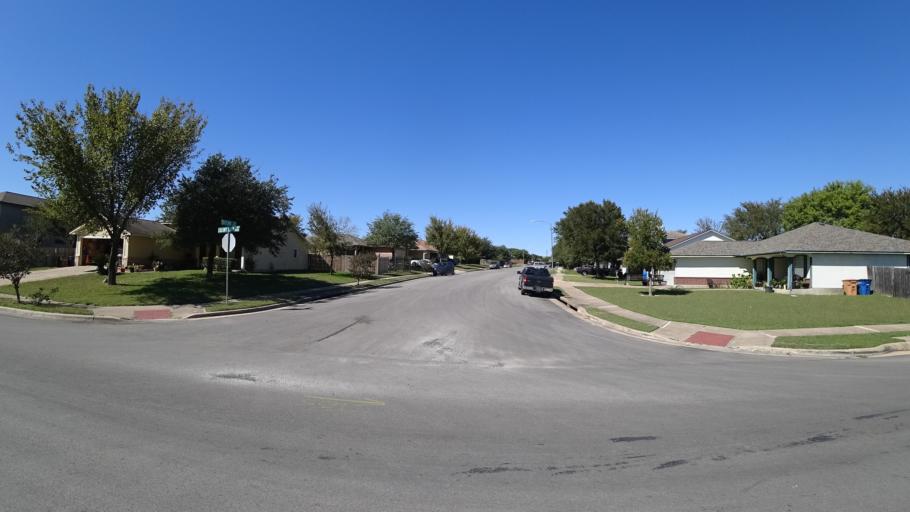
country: US
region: Texas
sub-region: Travis County
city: Hornsby Bend
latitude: 30.3021
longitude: -97.6378
